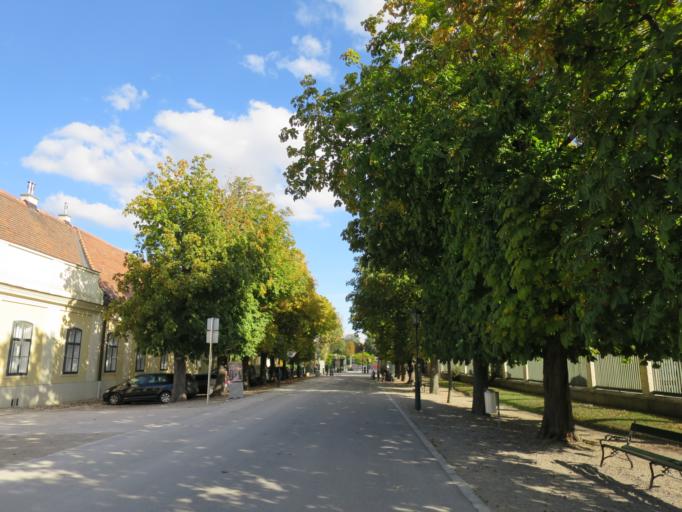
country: AT
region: Vienna
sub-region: Wien Stadt
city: Vienna
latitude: 48.1842
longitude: 16.3175
